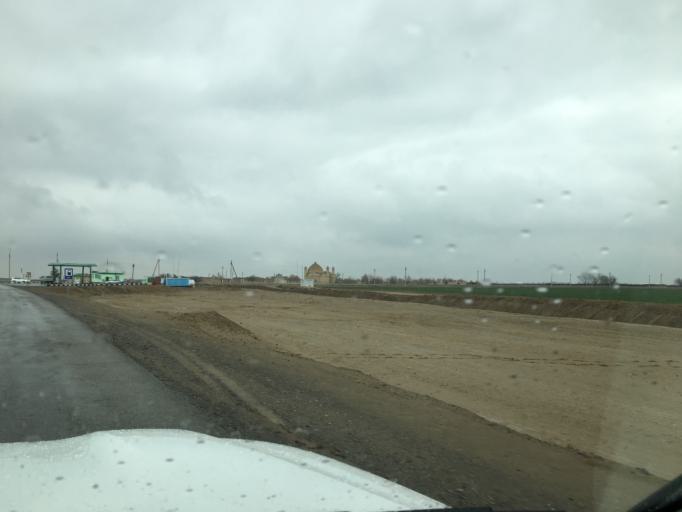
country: TM
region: Mary
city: Bayramaly
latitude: 37.4078
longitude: 62.1708
